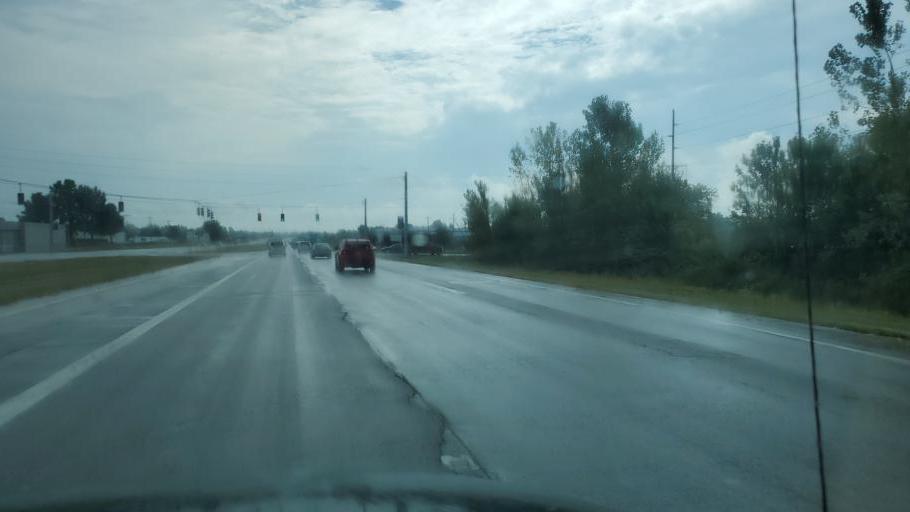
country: US
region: Ohio
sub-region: Licking County
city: Hebron
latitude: 39.9705
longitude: -82.4872
